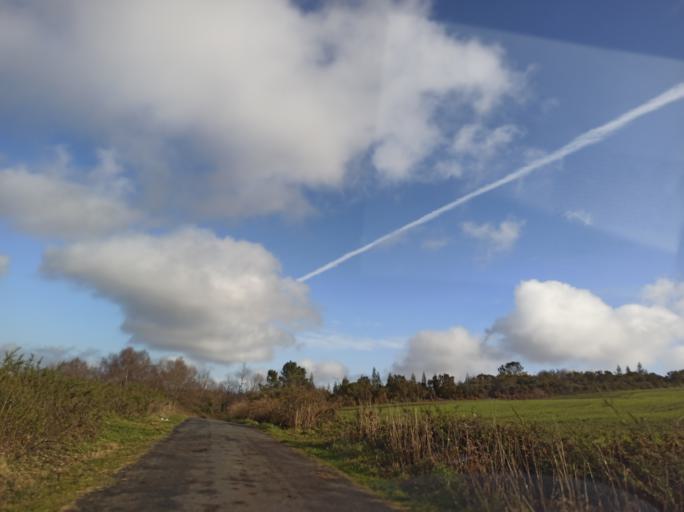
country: ES
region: Galicia
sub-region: Provincia da Coruna
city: Sobrado
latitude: 43.0796
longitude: -7.9516
